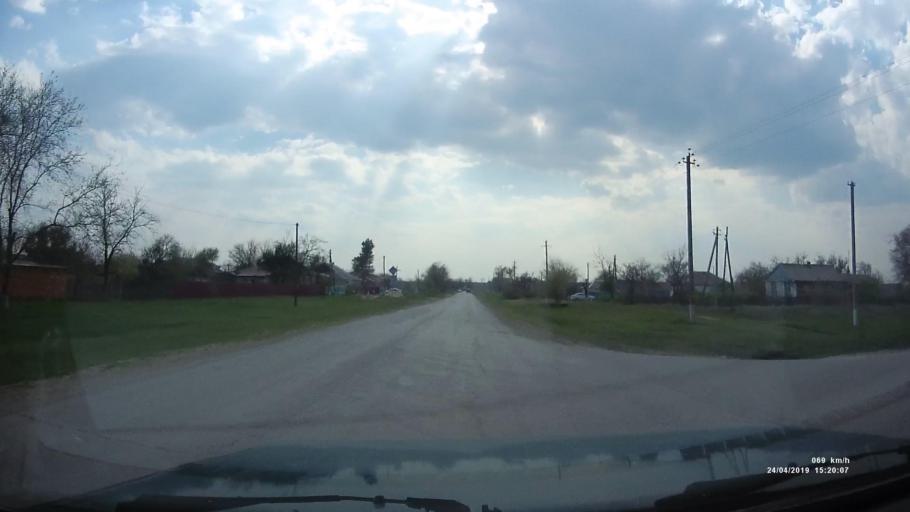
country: RU
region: Rostov
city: Remontnoye
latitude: 46.5366
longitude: 43.1364
